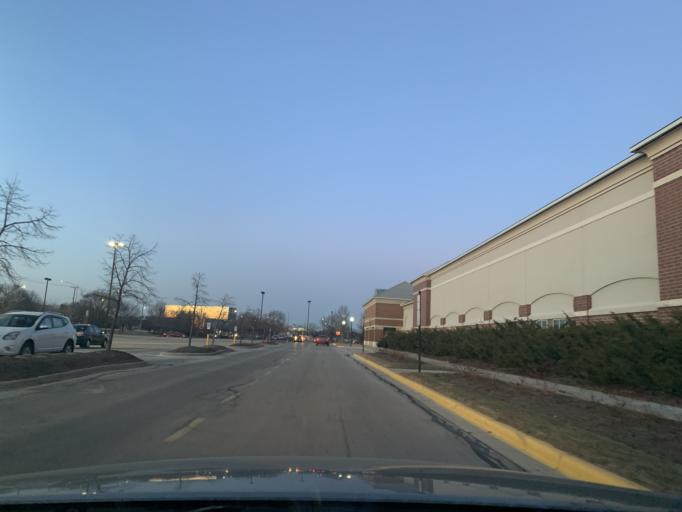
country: US
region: Illinois
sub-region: Cook County
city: Hoffman Estates
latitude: 42.0523
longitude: -88.0440
